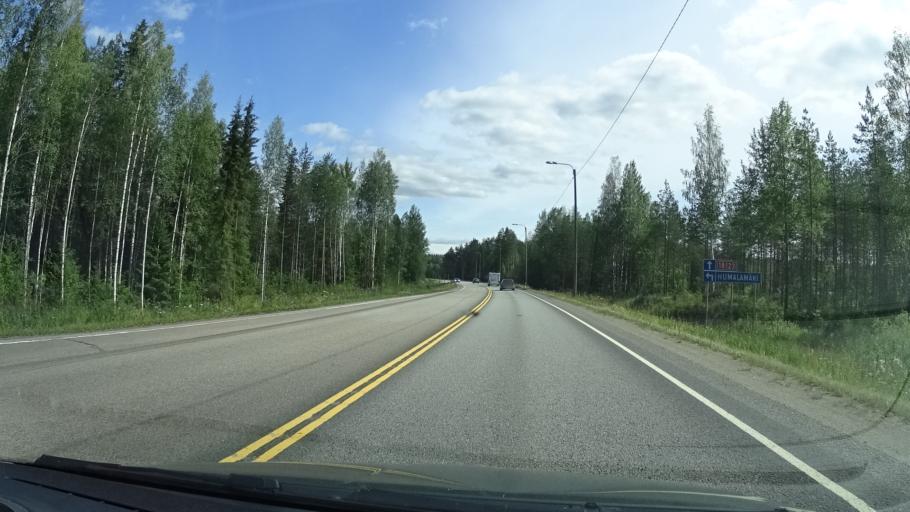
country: FI
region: Central Finland
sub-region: Jyvaeskylae
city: Muurame
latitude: 62.2671
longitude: 25.5225
